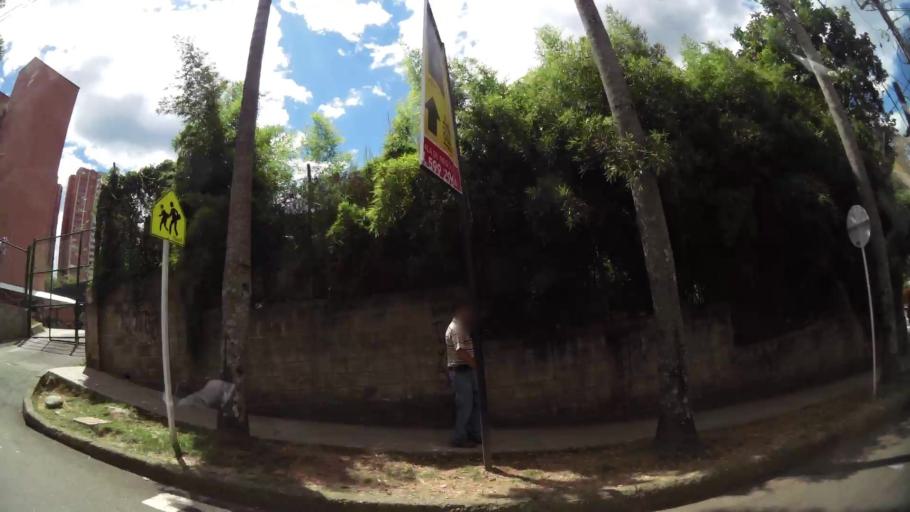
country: CO
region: Antioquia
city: Sabaneta
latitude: 6.1461
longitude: -75.6210
